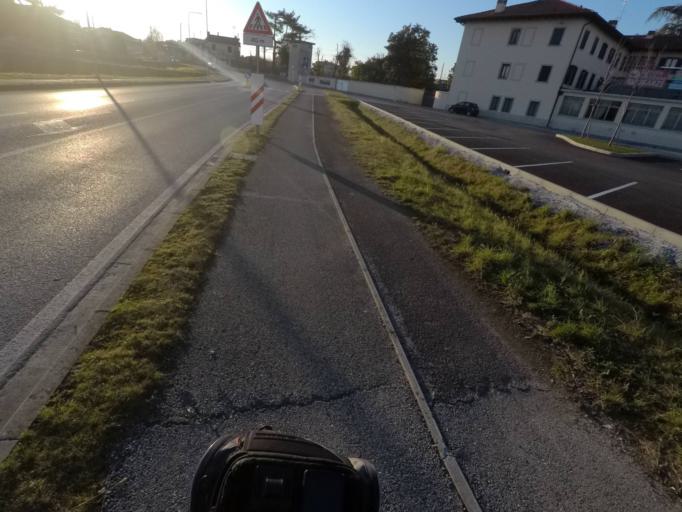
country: IT
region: Friuli Venezia Giulia
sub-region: Provincia di Udine
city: Udine
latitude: 46.0777
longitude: 13.2499
